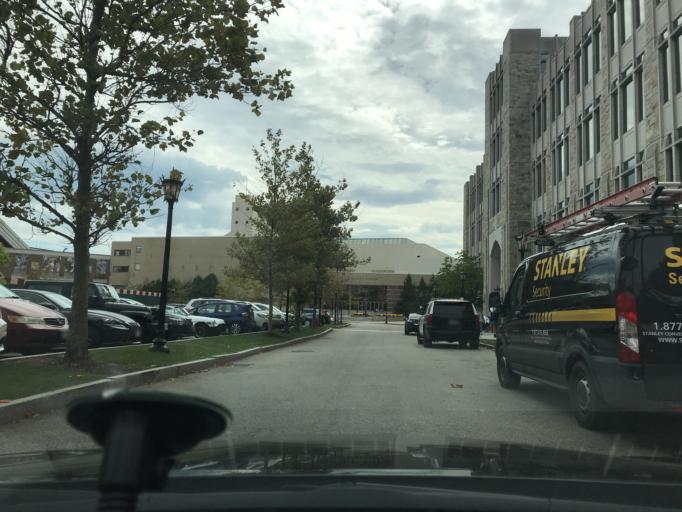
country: US
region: Massachusetts
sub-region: Middlesex County
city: Watertown
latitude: 42.3368
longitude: -71.1684
